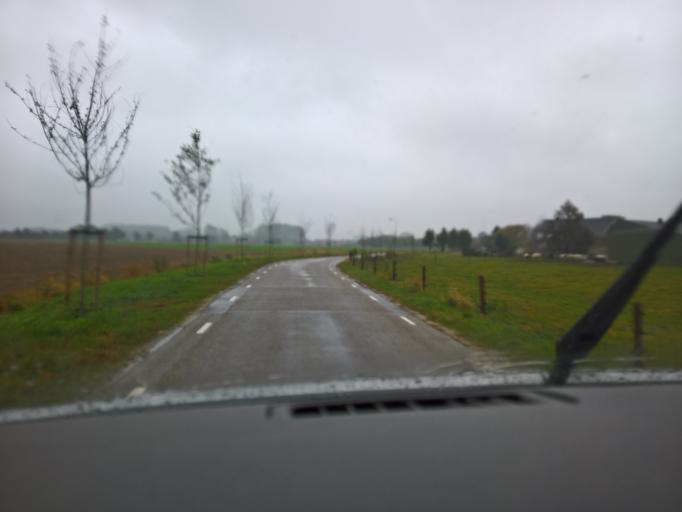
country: NL
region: Gelderland
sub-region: Gemeente Nijmegen
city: Lindenholt
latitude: 51.8574
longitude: 5.7924
